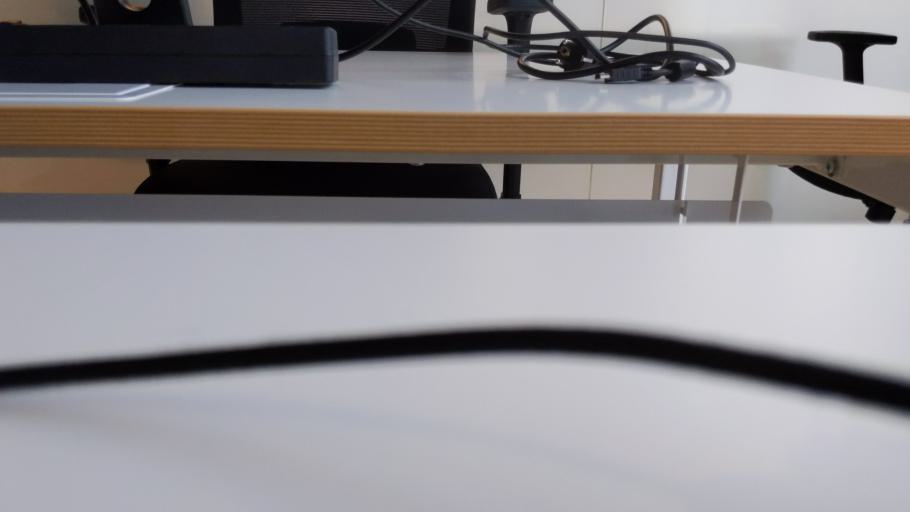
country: RU
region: Moskovskaya
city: Shevlyakovo
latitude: 56.4044
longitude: 36.8996
